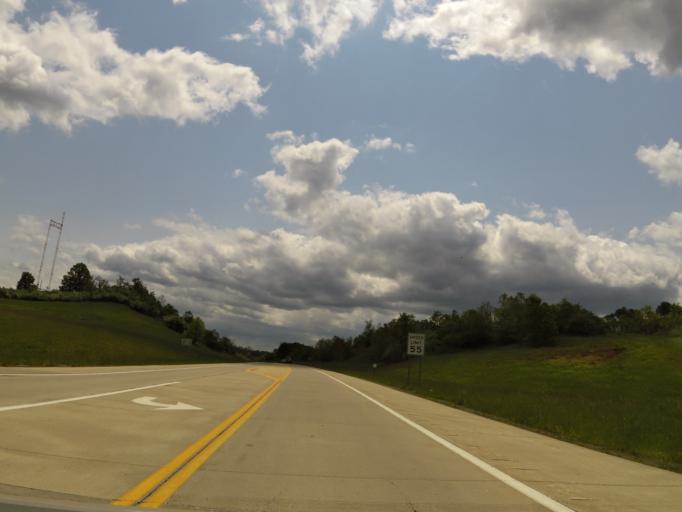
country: US
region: Ohio
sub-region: Athens County
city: Athens
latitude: 39.2380
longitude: -82.0744
